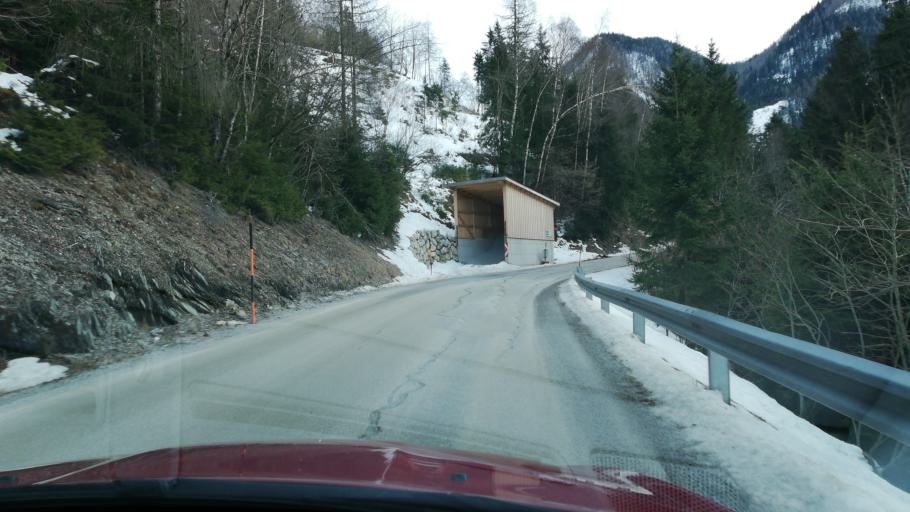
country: AT
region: Styria
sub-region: Politischer Bezirk Liezen
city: Donnersbach
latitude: 47.4425
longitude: 14.1400
